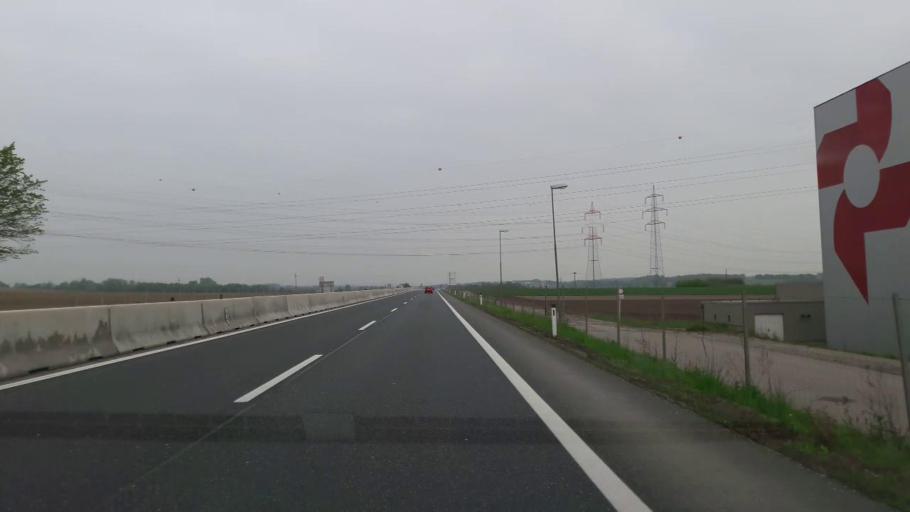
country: AT
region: Lower Austria
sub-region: Politischer Bezirk Korneuburg
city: Sierndorf
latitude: 48.3947
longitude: 16.1757
